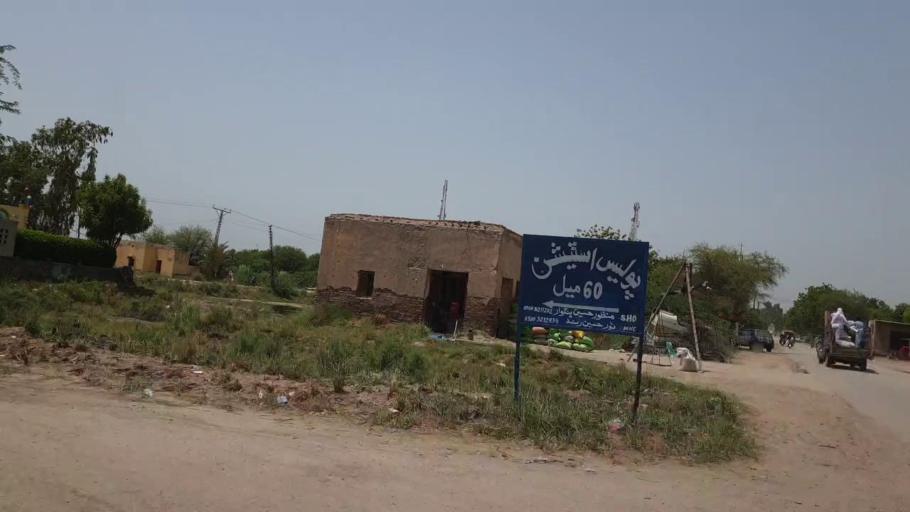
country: PK
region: Sindh
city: Daur
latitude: 26.3969
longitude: 68.4391
